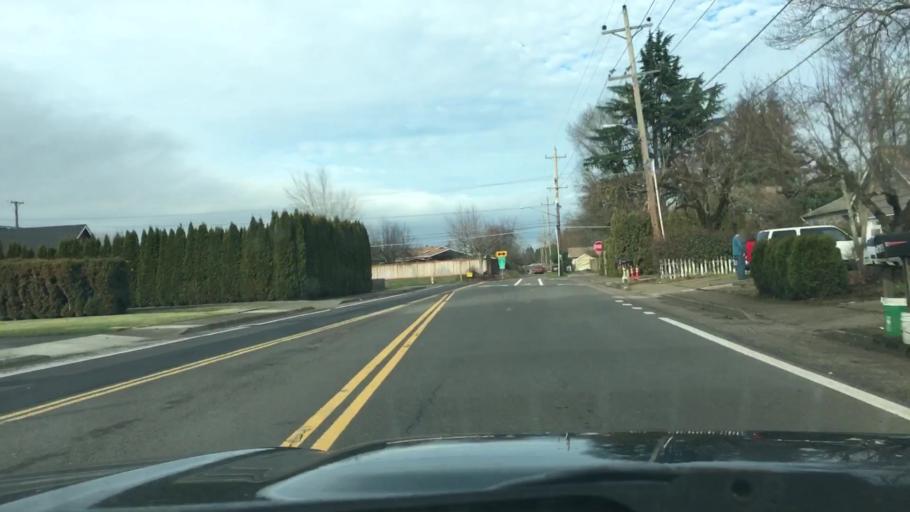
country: US
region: Oregon
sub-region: Lane County
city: Eugene
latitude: 44.0691
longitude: -123.1630
